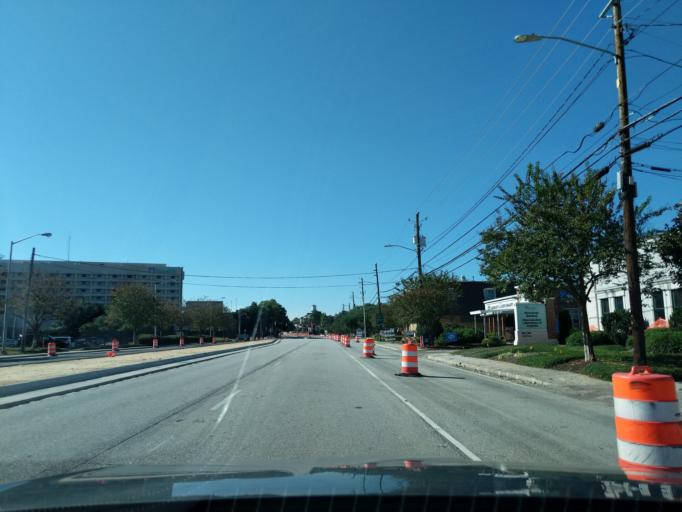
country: US
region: Georgia
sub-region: Richmond County
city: Augusta
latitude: 33.4741
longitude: -81.9887
